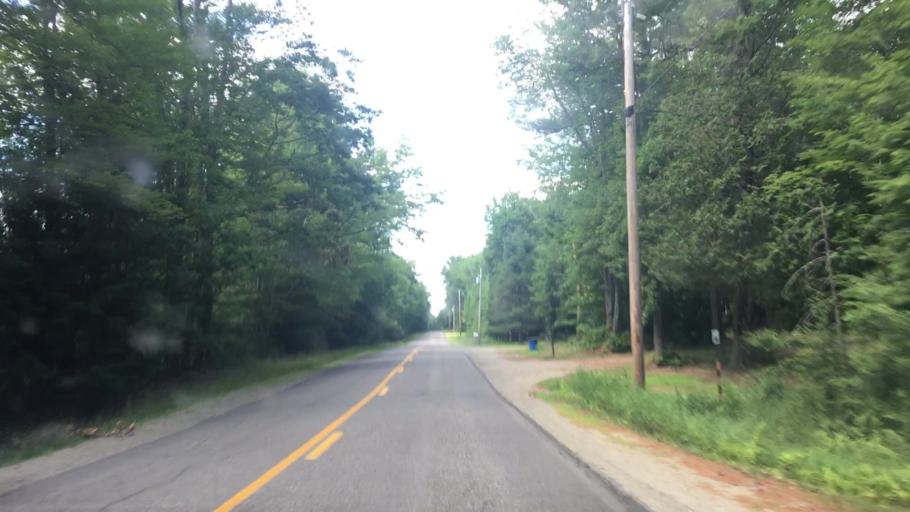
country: US
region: Maine
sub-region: Franklin County
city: Chesterville
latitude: 44.6012
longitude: -70.0843
